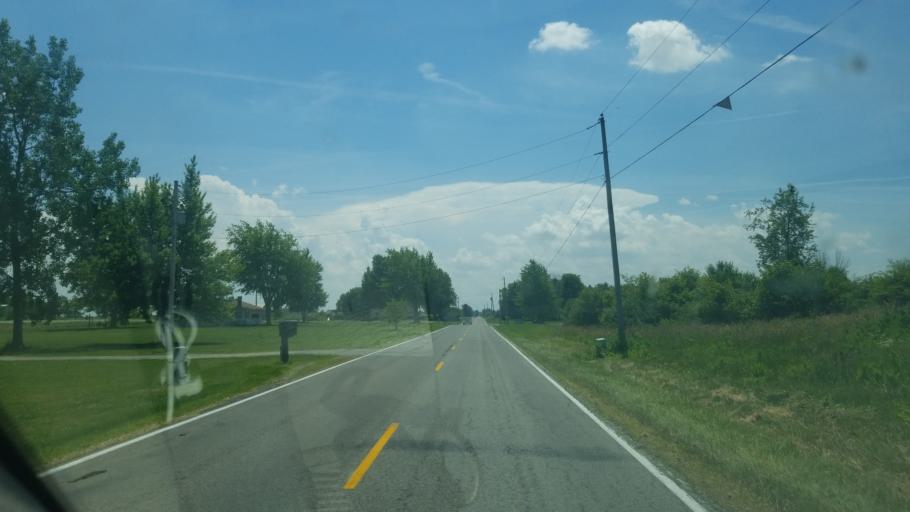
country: US
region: Ohio
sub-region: Hancock County
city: Arlington
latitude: 40.9532
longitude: -83.5941
